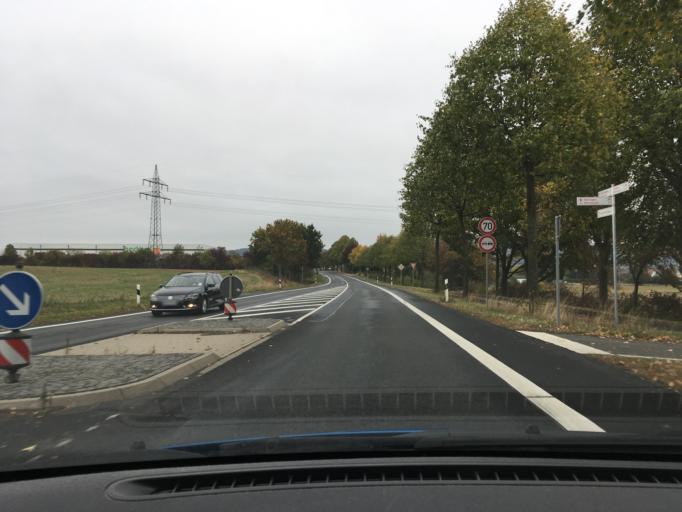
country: DE
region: Lower Saxony
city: Norten-Hardenberg
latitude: 51.6329
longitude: 9.9021
